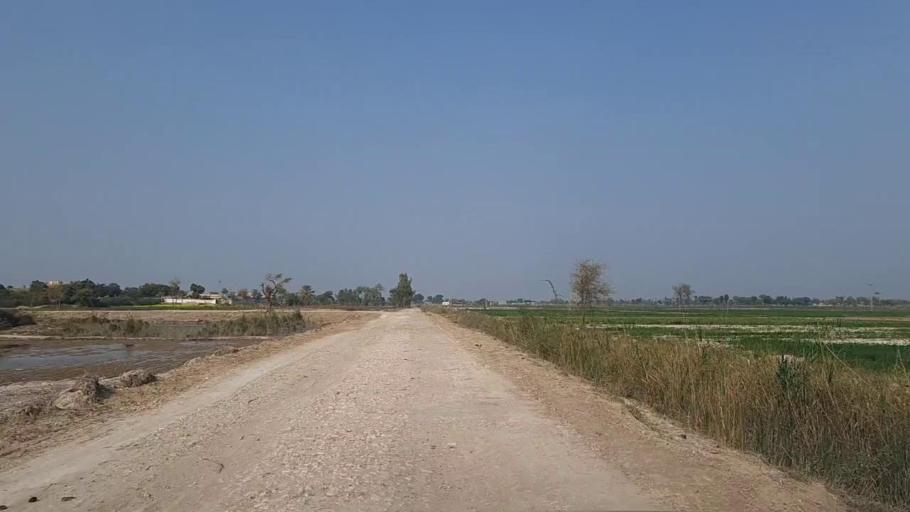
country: PK
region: Sindh
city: Daur
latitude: 26.3903
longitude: 68.4237
